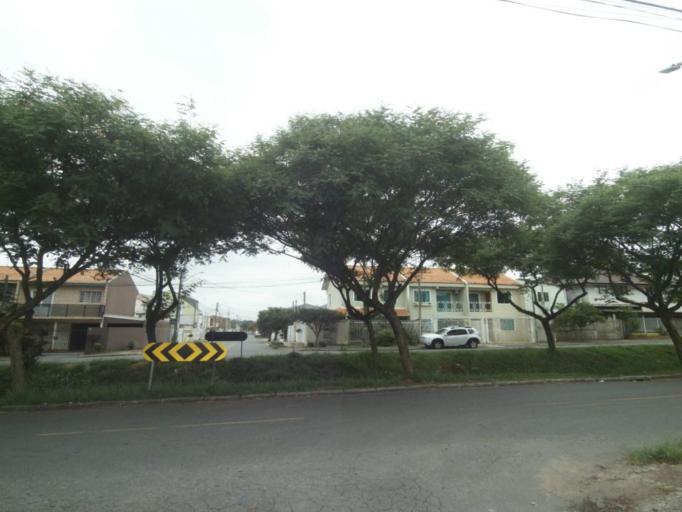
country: BR
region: Parana
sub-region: Araucaria
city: Araucaria
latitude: -25.5487
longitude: -49.3393
